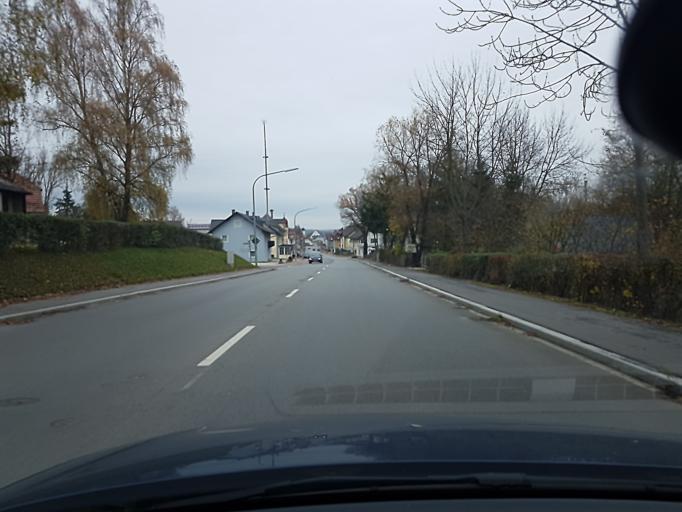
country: DE
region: Bavaria
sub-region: Lower Bavaria
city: Ergoldsbach
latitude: 48.7313
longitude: 12.1891
